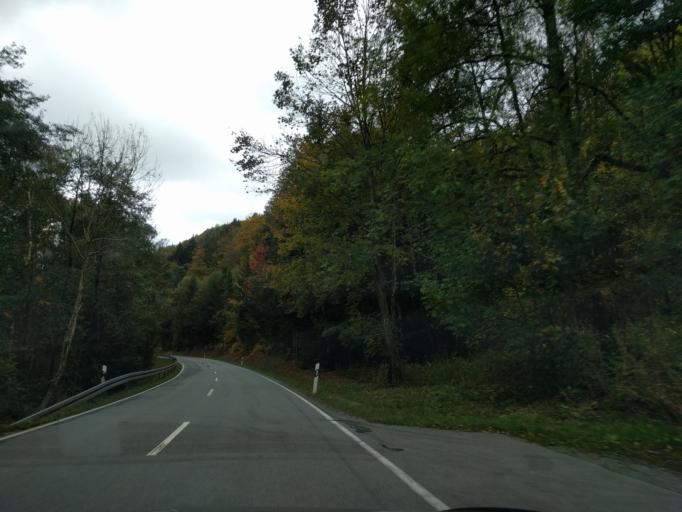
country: DE
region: Bavaria
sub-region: Lower Bavaria
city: Schaufling
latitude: 48.8742
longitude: 13.0848
